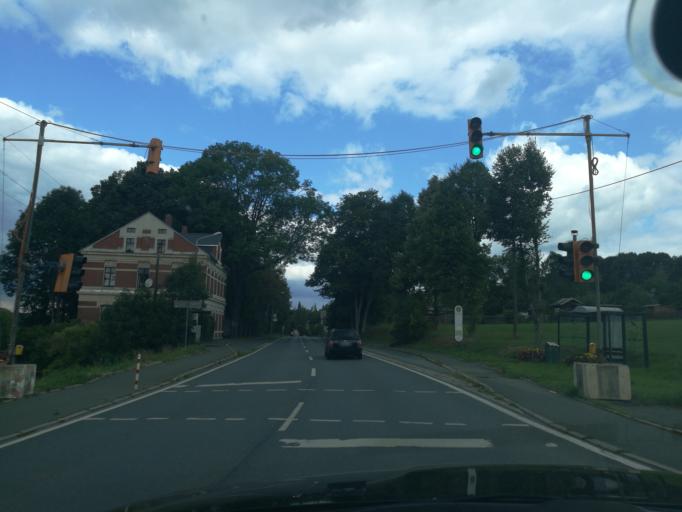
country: DE
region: Saxony
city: Oelsnitz
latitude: 50.4067
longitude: 12.1822
